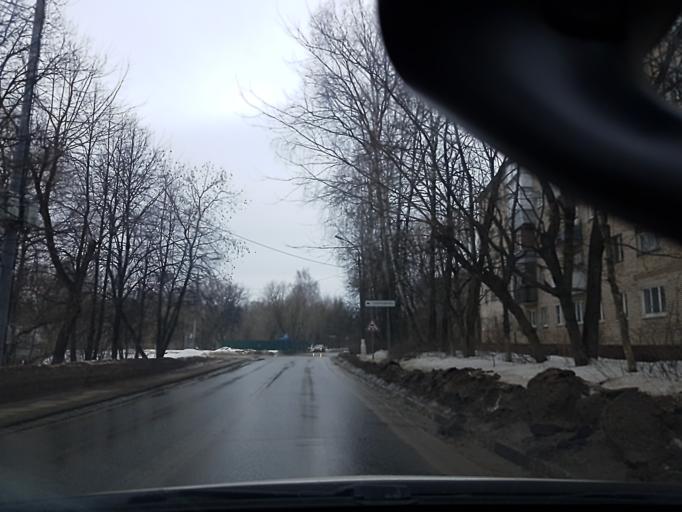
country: RU
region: Moskovskaya
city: Istra
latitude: 55.9063
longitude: 36.8677
